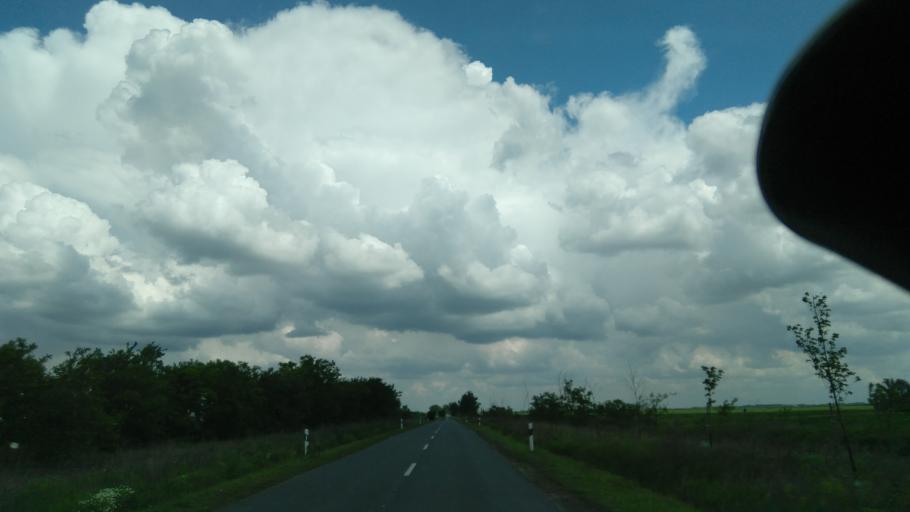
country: HU
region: Bekes
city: Devavanya
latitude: 46.9939
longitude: 20.9039
